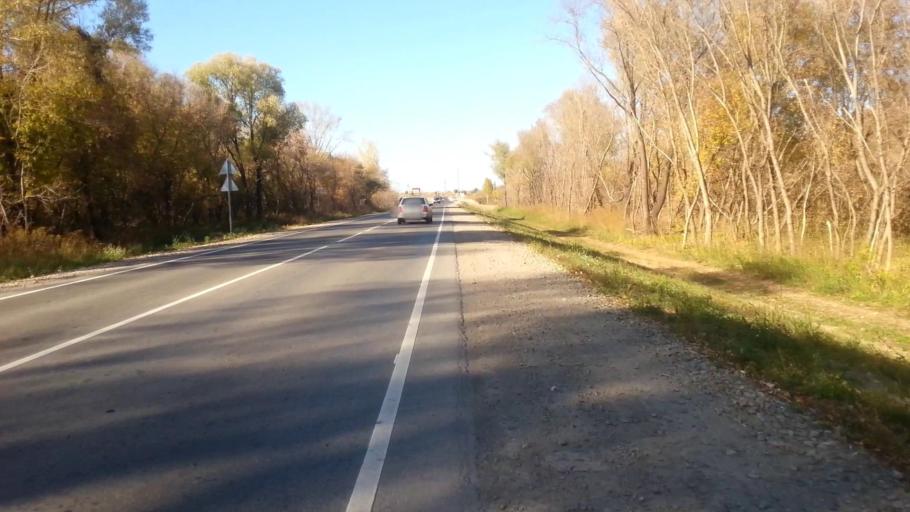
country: RU
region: Altai Krai
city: Sannikovo
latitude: 53.3242
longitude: 83.9427
